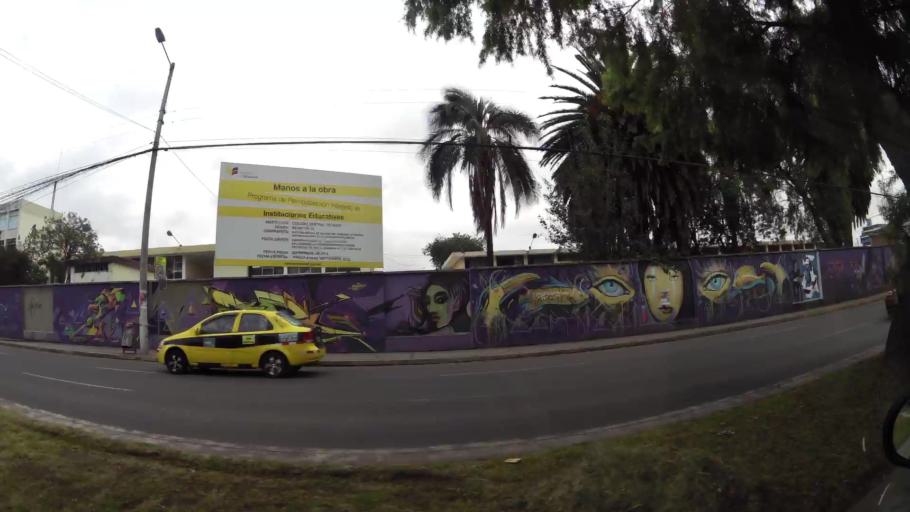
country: EC
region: Pichincha
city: Quito
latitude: -0.1698
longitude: -78.4820
